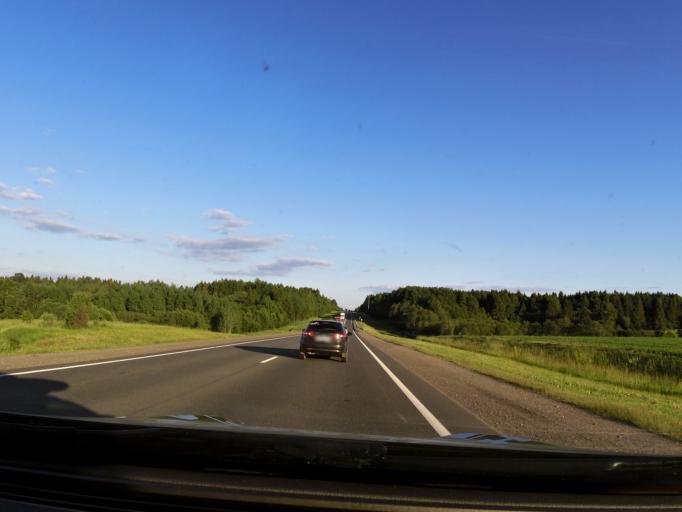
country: RU
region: Vologda
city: Vologda
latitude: 59.1380
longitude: 39.9511
